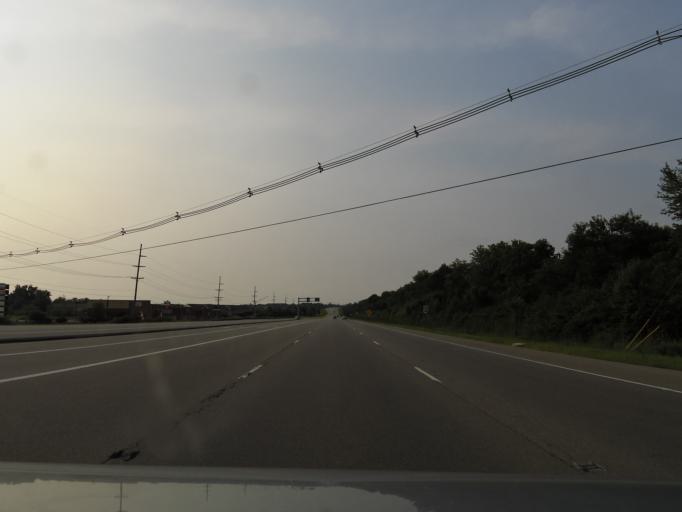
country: US
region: Ohio
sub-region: Butler County
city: Fairfield
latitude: 39.3631
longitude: -84.5041
